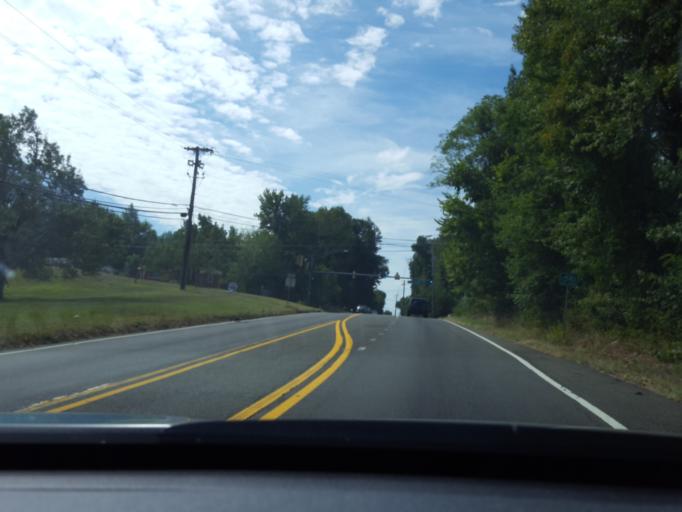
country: US
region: Maryland
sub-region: Prince George's County
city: Mellwood
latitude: 38.7950
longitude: -76.8355
